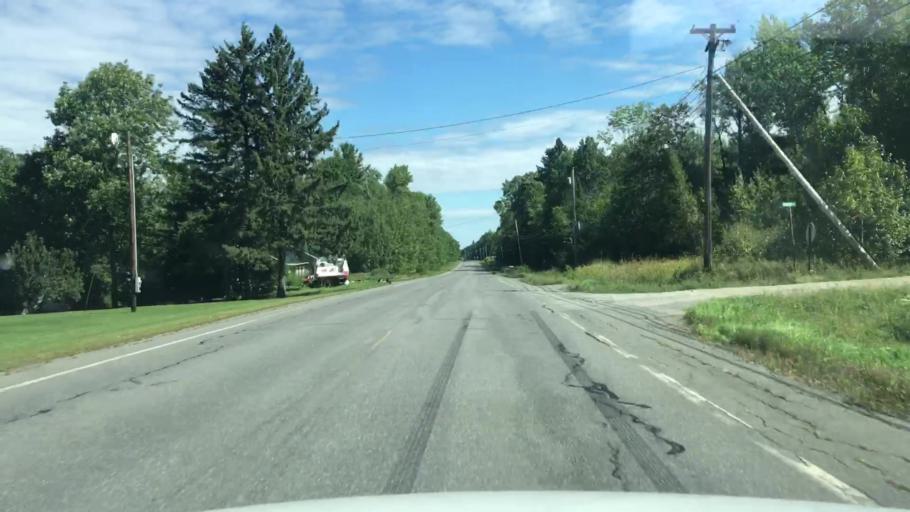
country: US
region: Maine
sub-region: Penobscot County
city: Dexter
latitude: 45.0626
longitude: -69.2473
